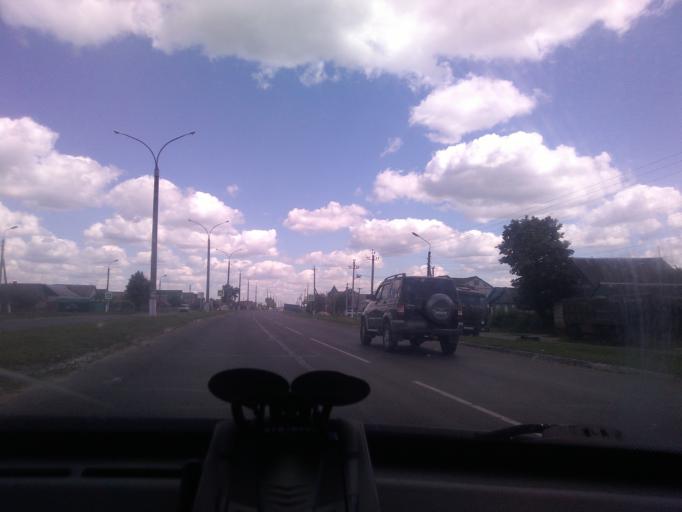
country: RU
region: Kursk
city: Pryamitsyno
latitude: 51.6576
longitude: 35.9486
